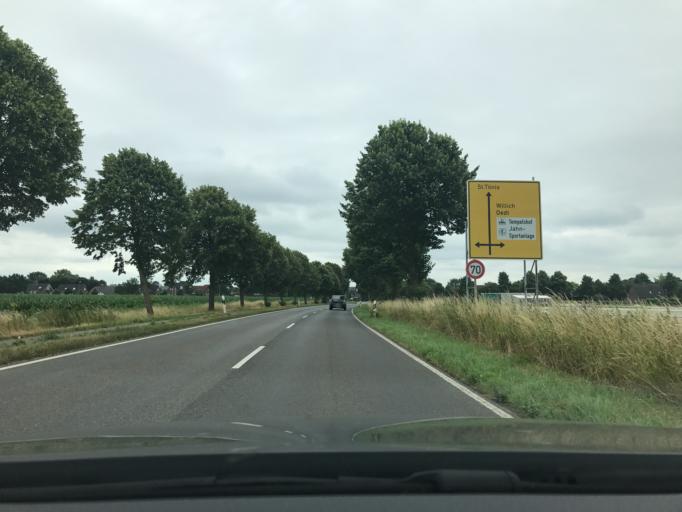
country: DE
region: North Rhine-Westphalia
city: Tonisvorst
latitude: 51.3325
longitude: 6.4940
